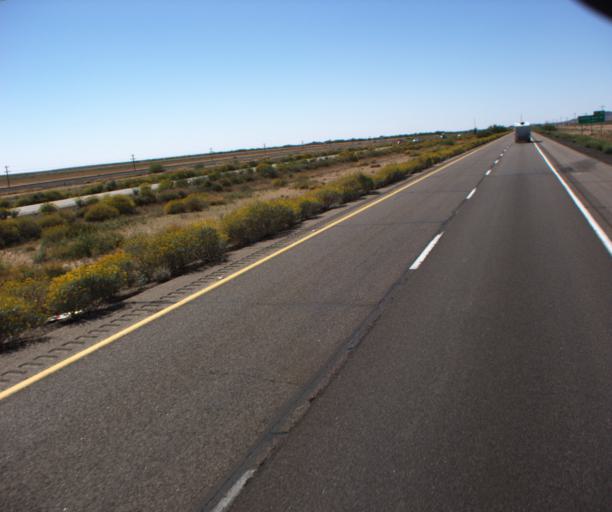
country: US
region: Arizona
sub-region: Maricopa County
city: Gila Bend
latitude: 32.9136
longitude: -112.9448
